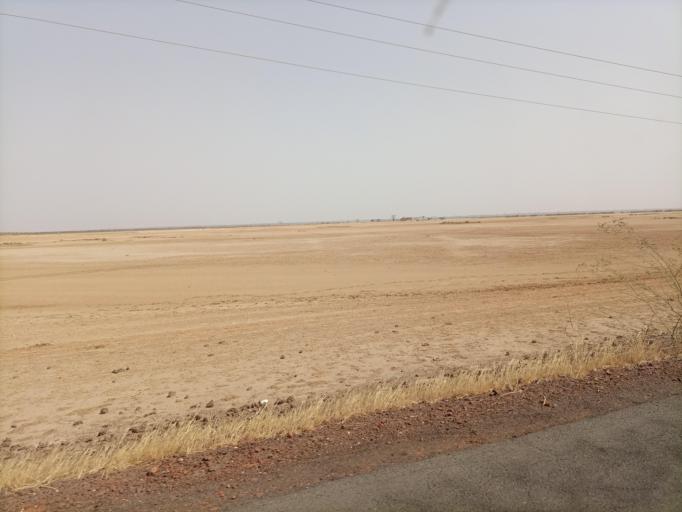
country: SN
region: Fatick
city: Foundiougne
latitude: 14.1715
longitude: -16.4608
